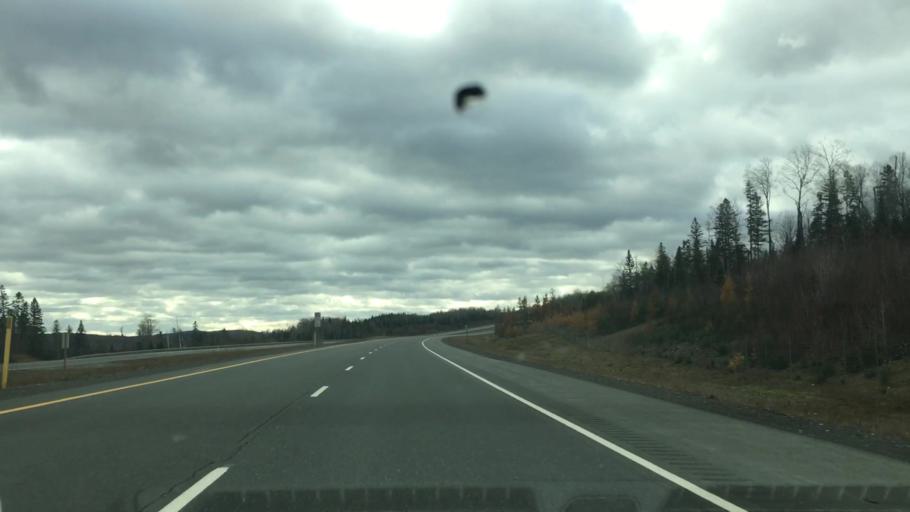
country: US
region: Maine
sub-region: Aroostook County
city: Fort Fairfield
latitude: 46.6726
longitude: -67.7294
